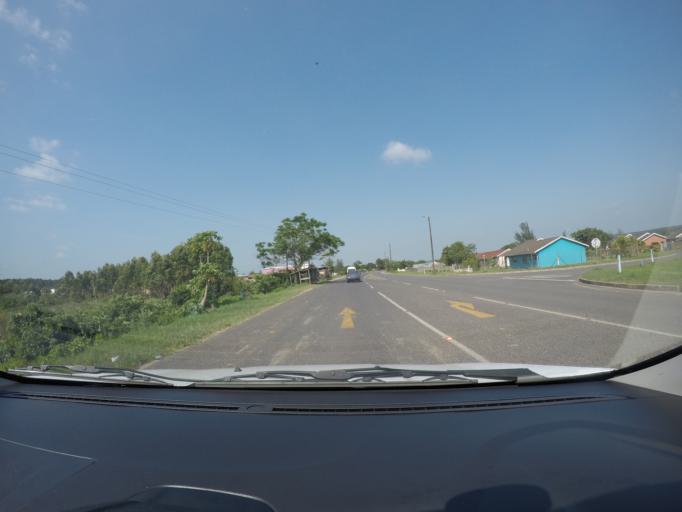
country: ZA
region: KwaZulu-Natal
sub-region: uThungulu District Municipality
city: eSikhawini
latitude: -28.8919
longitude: 31.8901
